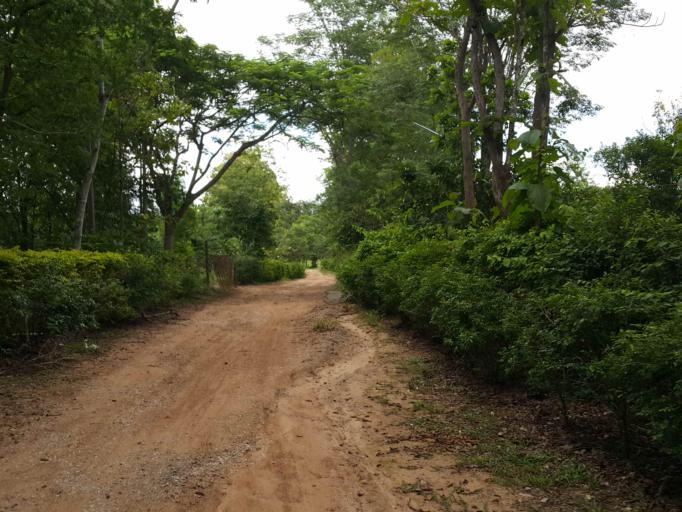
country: TH
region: Chiang Mai
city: San Sai
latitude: 18.9405
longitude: 98.9109
